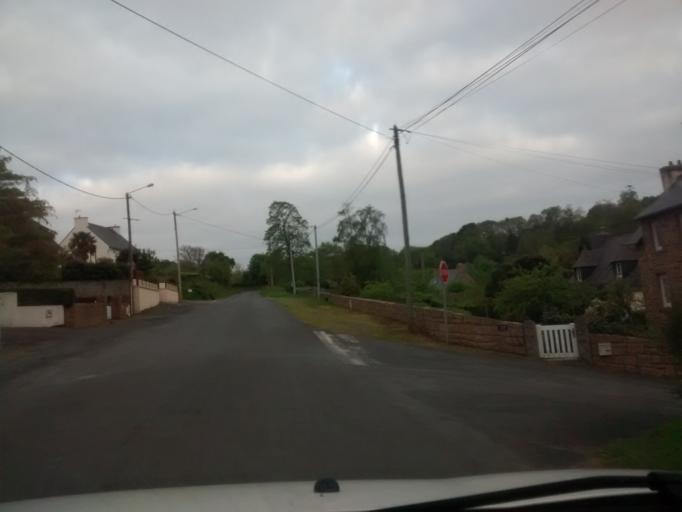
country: FR
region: Brittany
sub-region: Departement des Cotes-d'Armor
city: Saint-Quay-Perros
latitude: 48.7973
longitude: -3.4478
